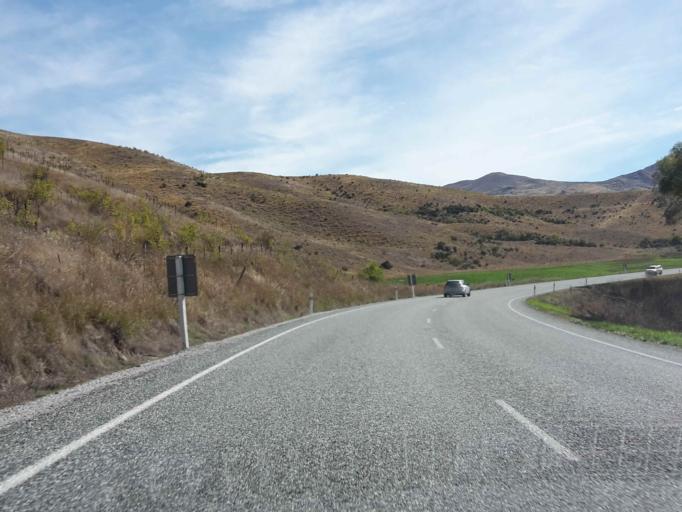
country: NZ
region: Otago
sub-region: Queenstown-Lakes District
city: Wanaka
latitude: -44.7947
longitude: 169.5050
